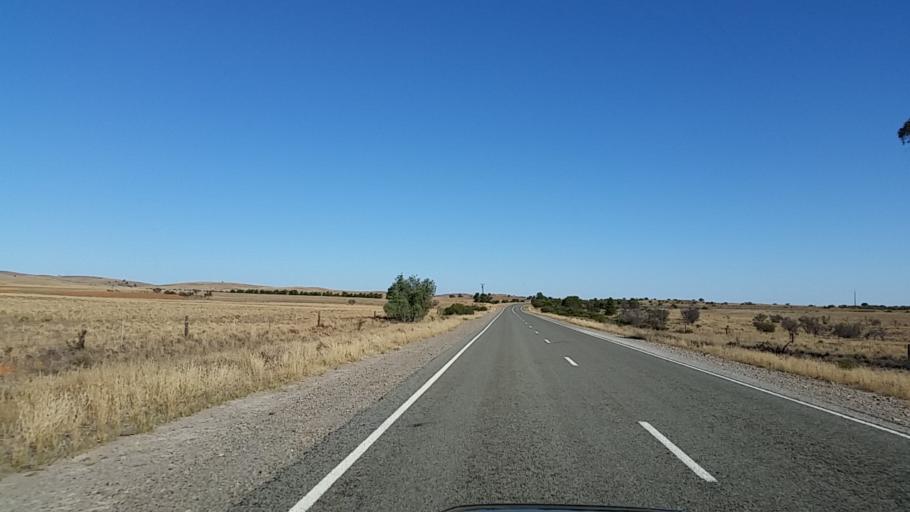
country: AU
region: South Australia
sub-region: Peterborough
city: Peterborough
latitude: -32.5401
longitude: 138.5585
